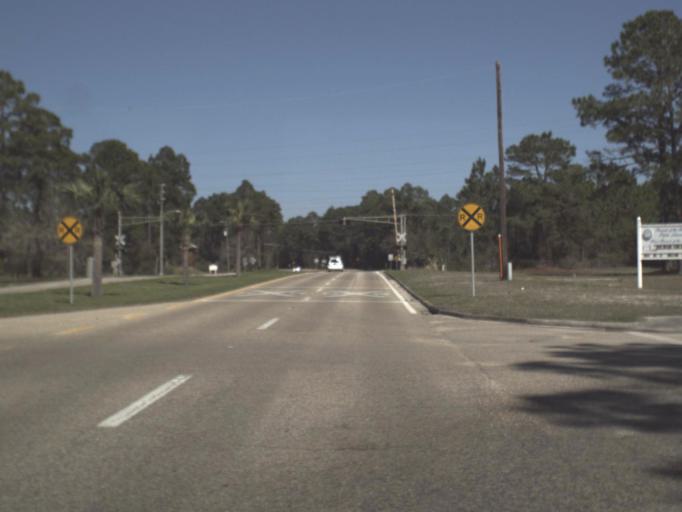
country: US
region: Florida
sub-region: Gulf County
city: Port Saint Joe
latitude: 29.8158
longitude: -85.2896
